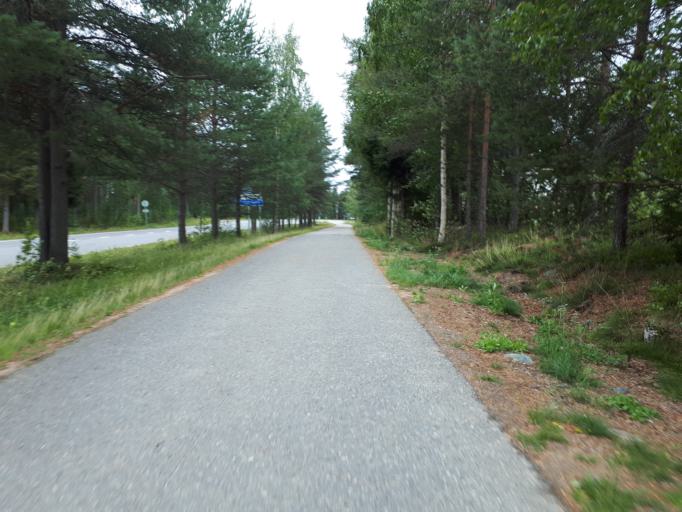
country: FI
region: Northern Ostrobothnia
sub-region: Oulunkaari
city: Ii
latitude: 65.3163
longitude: 25.3911
